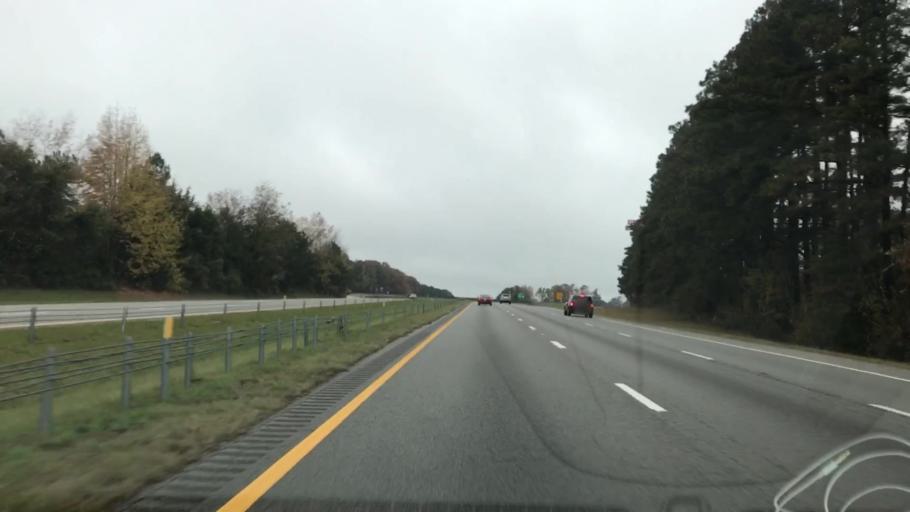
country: US
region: South Carolina
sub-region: Newberry County
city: Prosperity
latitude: 34.2375
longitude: -81.4559
